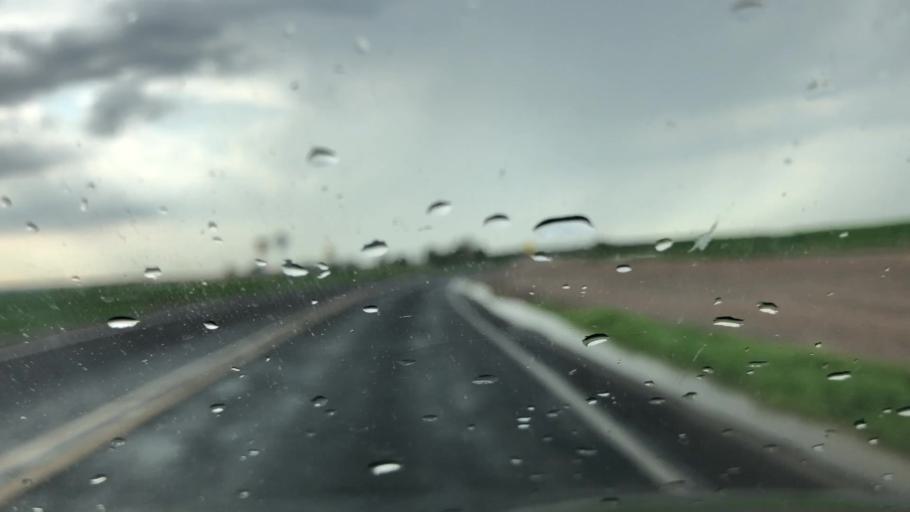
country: US
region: New Mexico
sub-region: Dona Ana County
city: Vado
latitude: 32.0651
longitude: -106.6790
